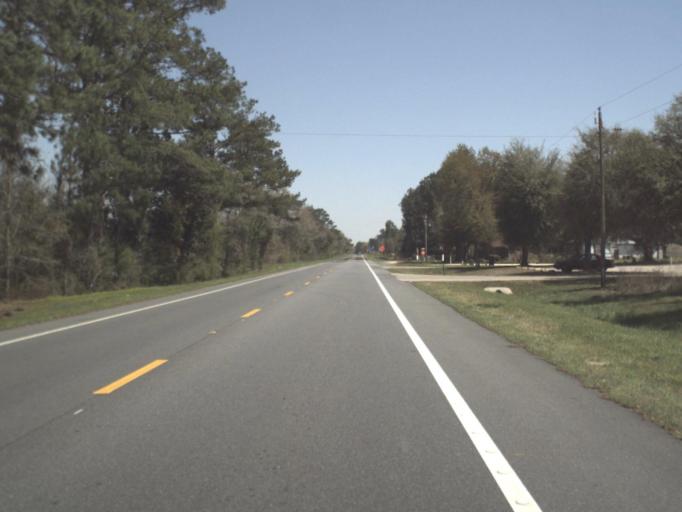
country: US
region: Florida
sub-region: Calhoun County
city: Blountstown
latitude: 30.4368
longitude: -85.2020
